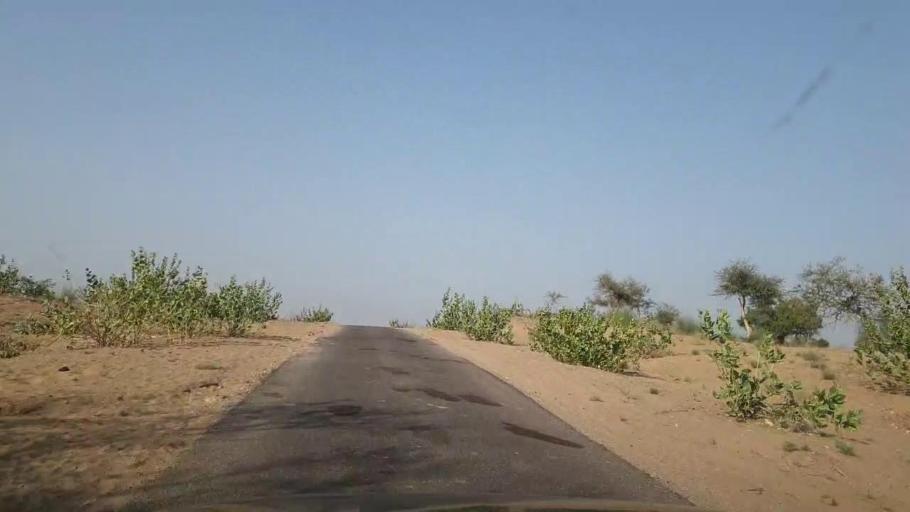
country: PK
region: Sindh
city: Islamkot
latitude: 25.1481
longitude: 70.5196
